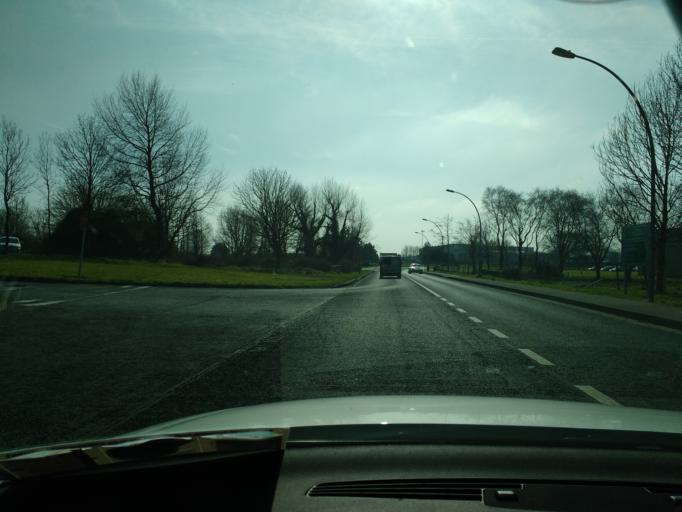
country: IE
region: Munster
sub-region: An Clar
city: Shannon
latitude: 52.6989
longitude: -8.8999
